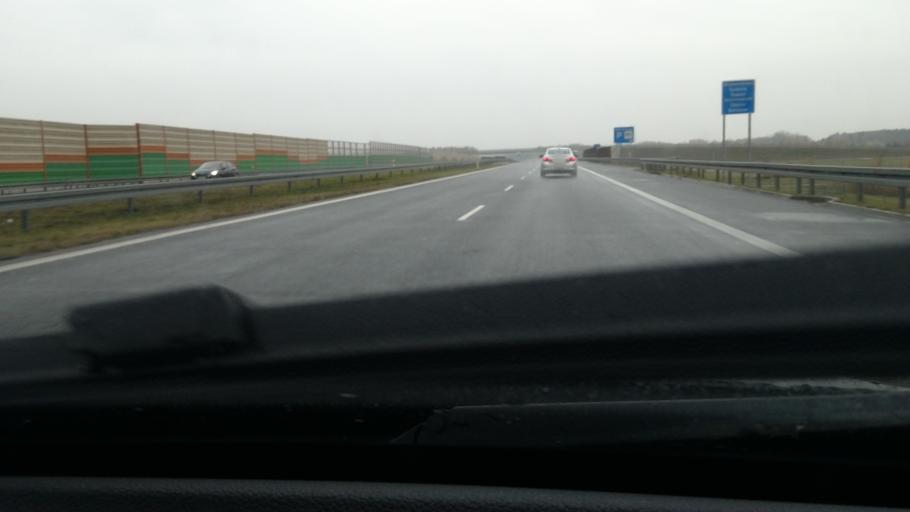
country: PL
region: Lodz Voivodeship
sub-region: Powiat skierniewicki
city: Bolimow
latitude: 52.0747
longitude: 20.2469
